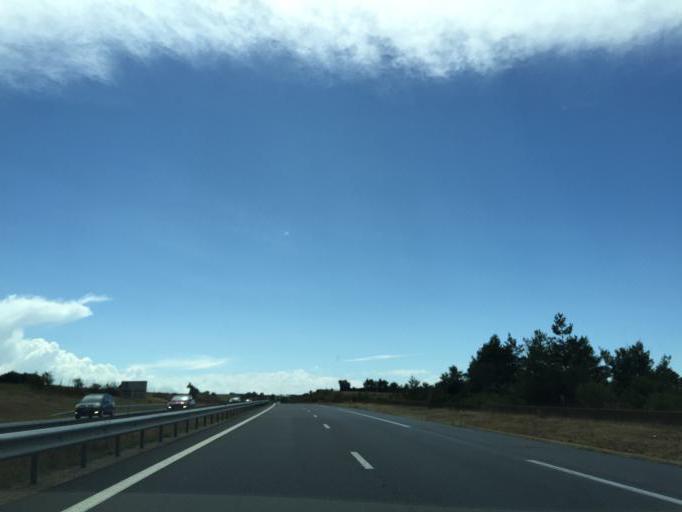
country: FR
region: Midi-Pyrenees
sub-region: Departement de l'Aveyron
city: Severac-le-Chateau
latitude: 44.2878
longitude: 3.0940
